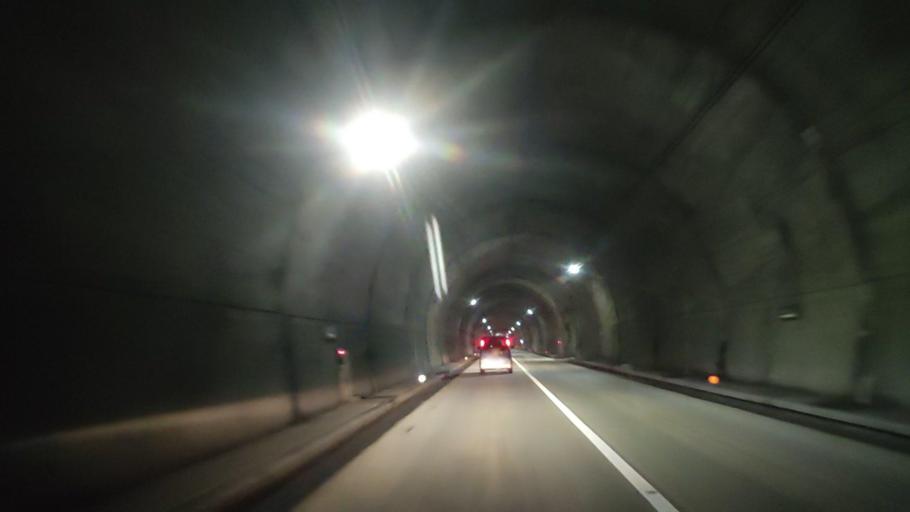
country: JP
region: Gifu
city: Takayama
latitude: 36.1821
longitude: 137.5349
